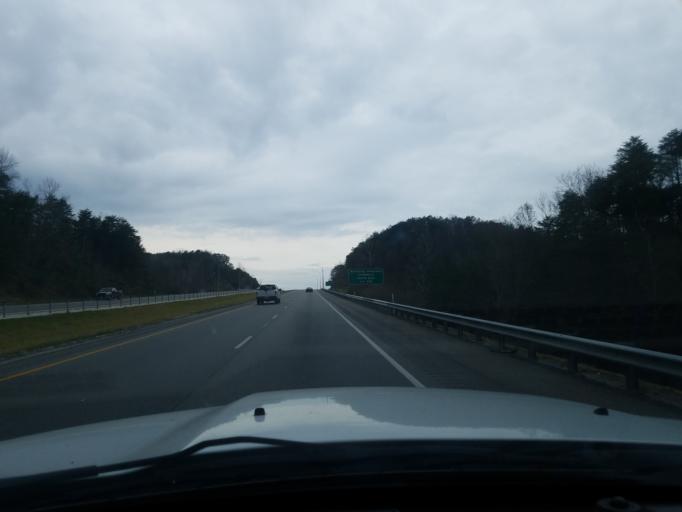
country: US
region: Kentucky
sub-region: Boyd County
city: Meads
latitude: 38.3657
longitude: -82.8127
